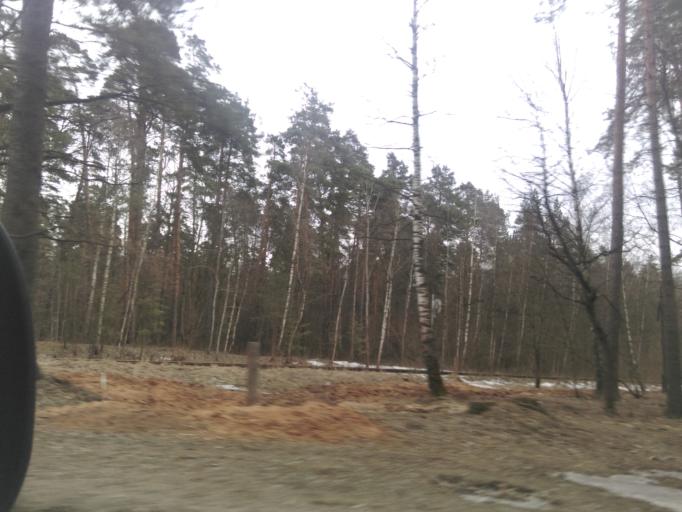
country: RU
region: Moscow
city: Rublevo
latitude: 55.7591
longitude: 37.3450
